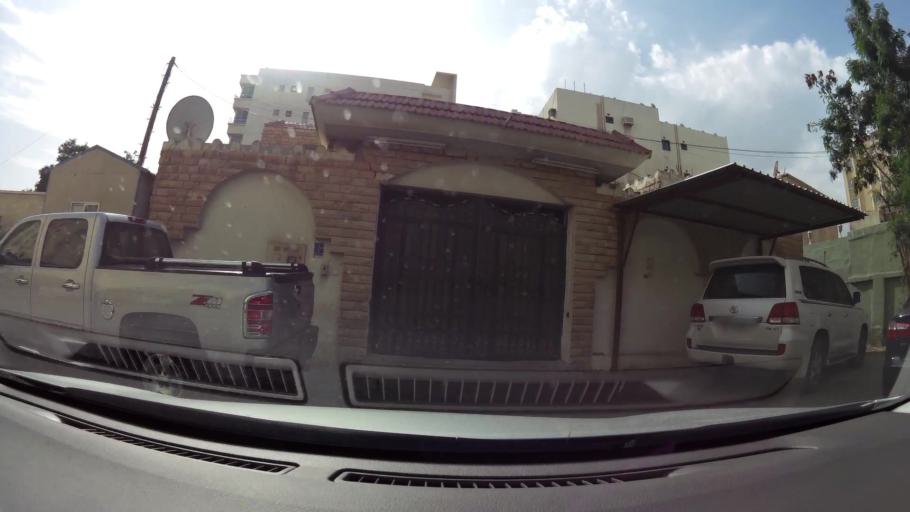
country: QA
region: Baladiyat ad Dawhah
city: Doha
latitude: 25.2814
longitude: 51.5127
